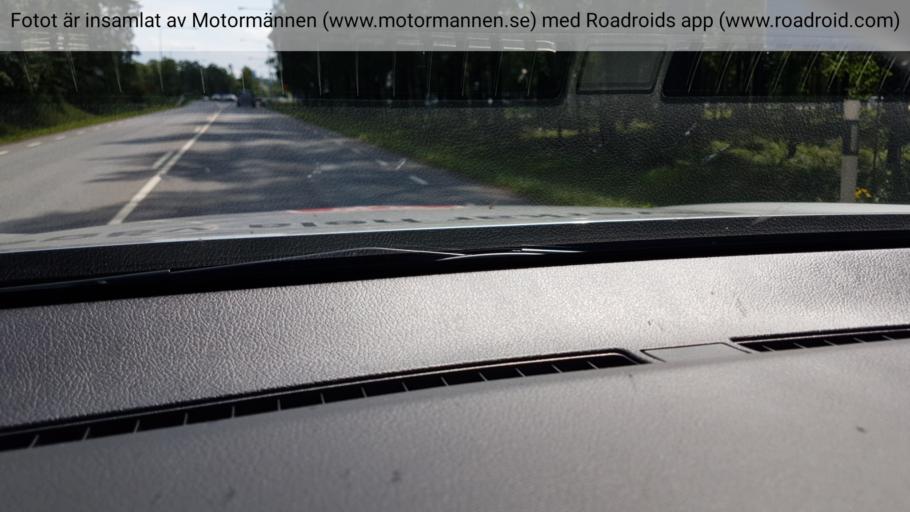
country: SE
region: Vaestra Goetaland
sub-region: Lidkopings Kommun
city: Lidkoping
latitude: 58.4945
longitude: 13.1381
